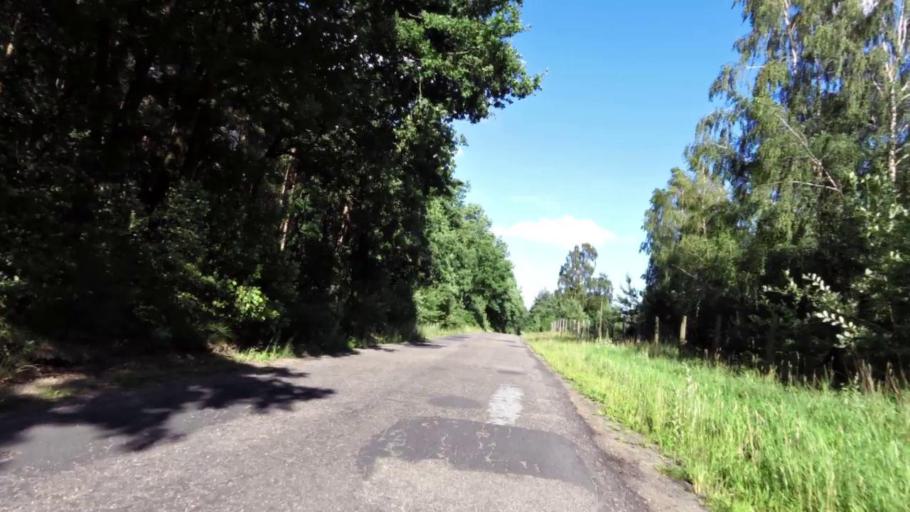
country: PL
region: West Pomeranian Voivodeship
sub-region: Powiat slawienski
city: Slawno
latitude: 54.4366
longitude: 16.7575
